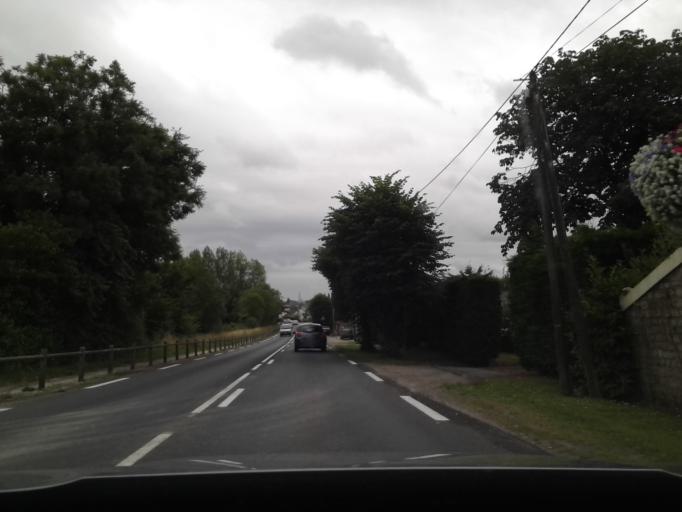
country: FR
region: Lower Normandy
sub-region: Departement de la Manche
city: Valognes
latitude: 49.5150
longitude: -1.4855
